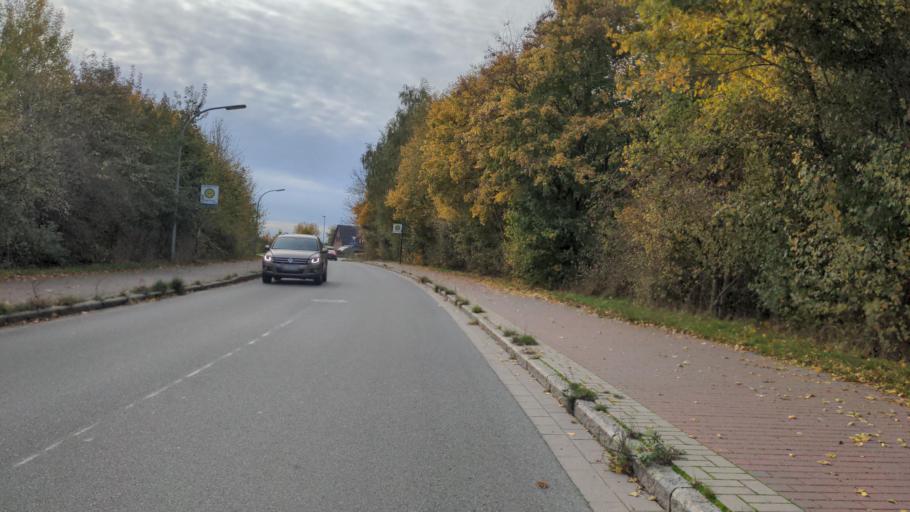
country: DE
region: Schleswig-Holstein
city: Stockelsdorf
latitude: 53.9092
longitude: 10.6634
